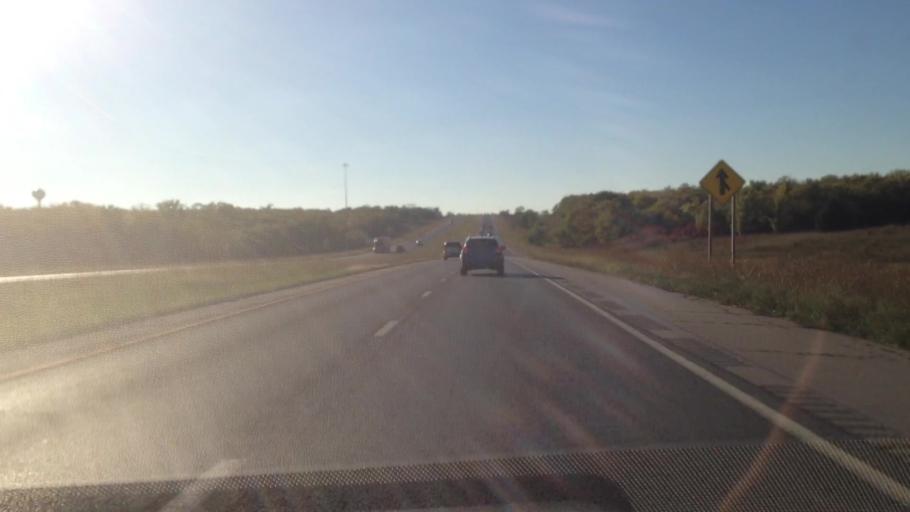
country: US
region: Kansas
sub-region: Johnson County
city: De Soto
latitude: 38.9611
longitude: -94.9862
